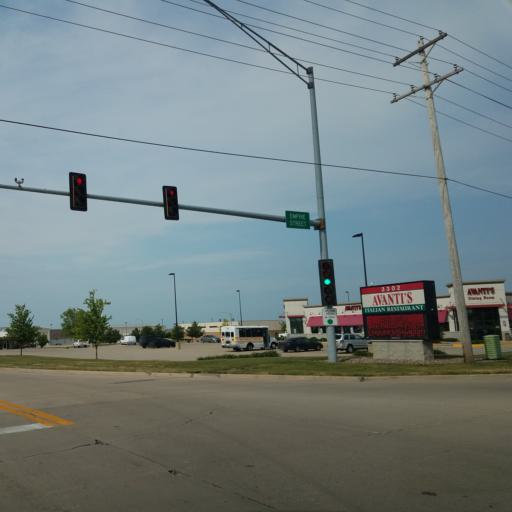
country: US
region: Illinois
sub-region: McLean County
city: Bloomington
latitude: 40.4883
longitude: -88.9097
